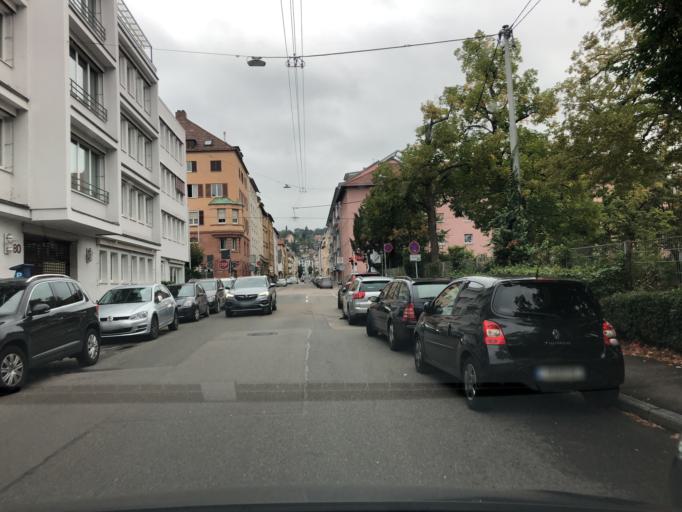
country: DE
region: Baden-Wuerttemberg
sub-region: Regierungsbezirk Stuttgart
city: Stuttgart
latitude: 48.7799
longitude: 9.1622
